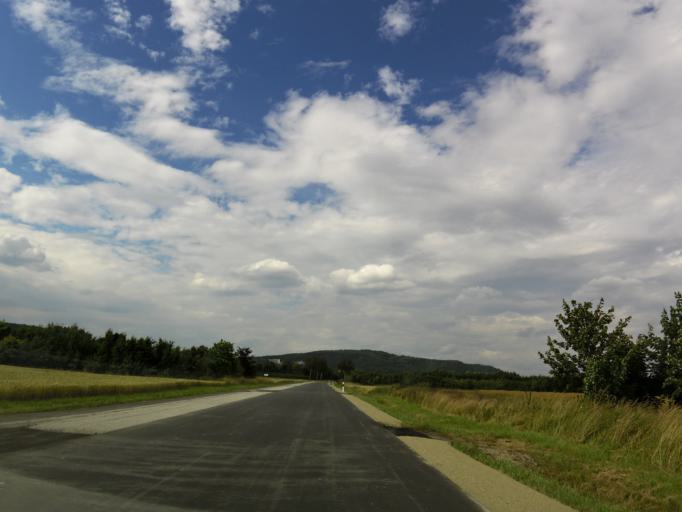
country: DE
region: Lower Saxony
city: Boffzen
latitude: 51.7623
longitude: 9.3876
